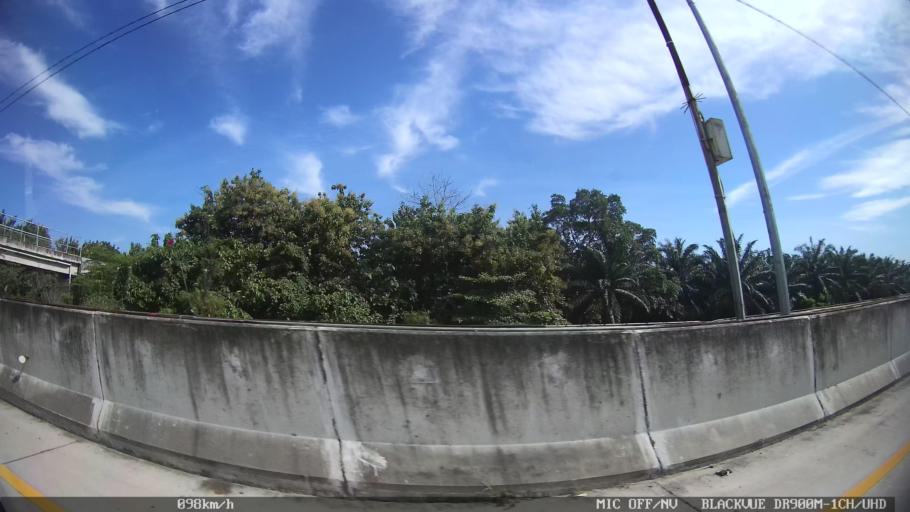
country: ID
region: North Sumatra
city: Sunggal
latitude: 3.6384
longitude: 98.6130
